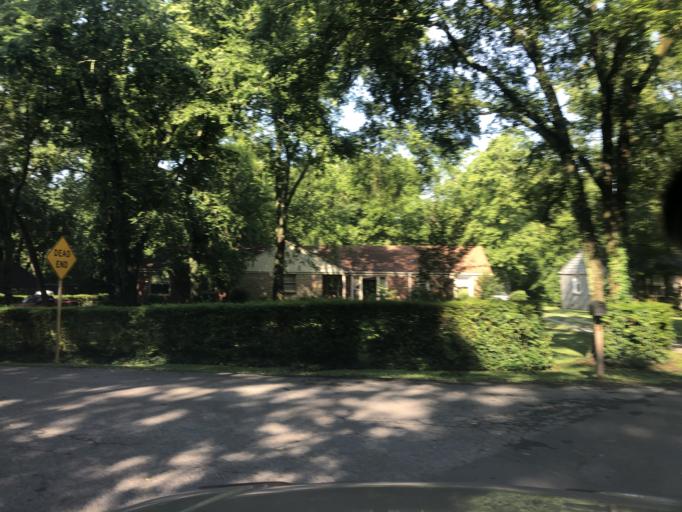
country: US
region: Tennessee
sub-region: Davidson County
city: Lakewood
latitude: 36.2279
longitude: -86.7141
